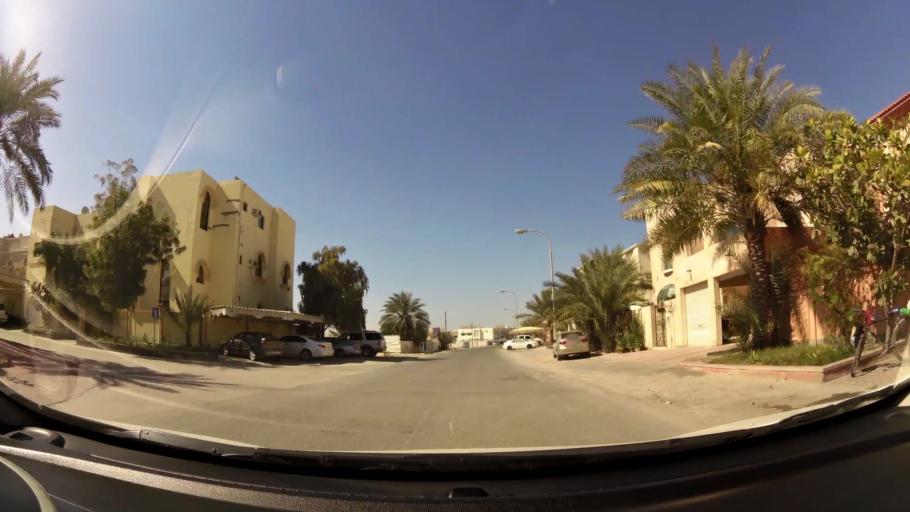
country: BH
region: Muharraq
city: Al Hadd
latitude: 26.2452
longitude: 50.6328
